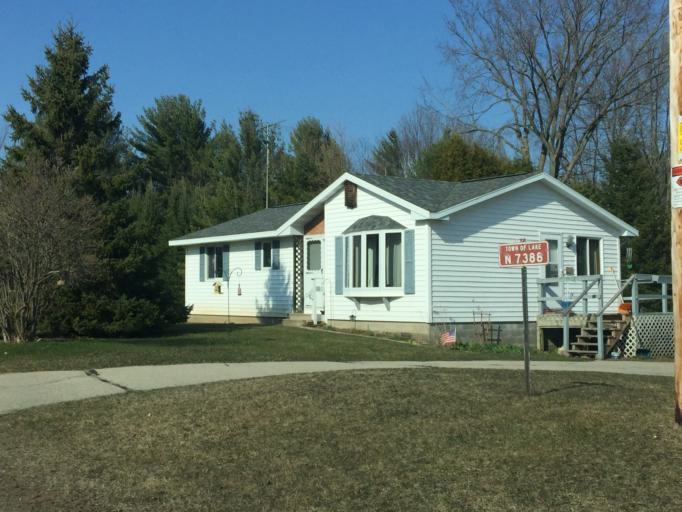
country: US
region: Wisconsin
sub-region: Marinette County
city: Peshtigo
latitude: 45.2253
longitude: -87.8618
